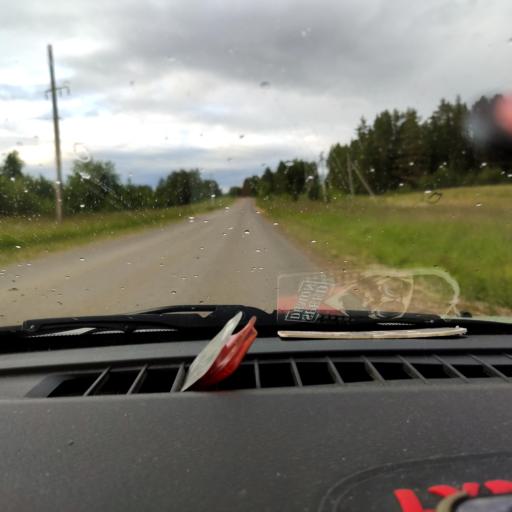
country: RU
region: Perm
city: Ocher
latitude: 57.9134
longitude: 54.7588
